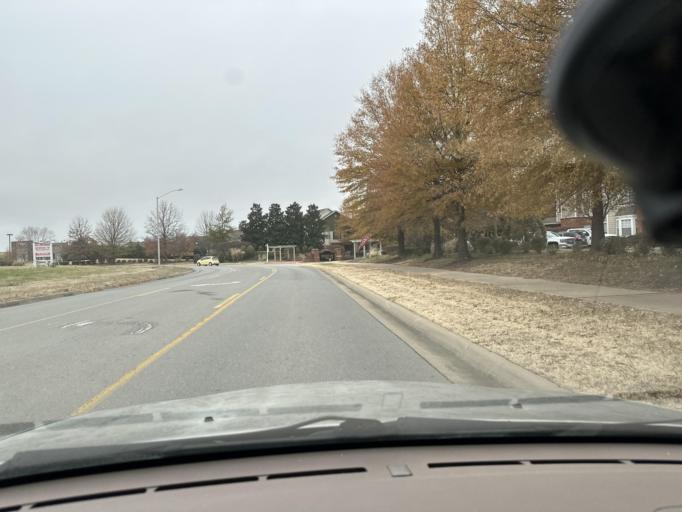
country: US
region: Arkansas
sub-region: Washington County
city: Johnson
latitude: 36.1275
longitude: -94.1539
